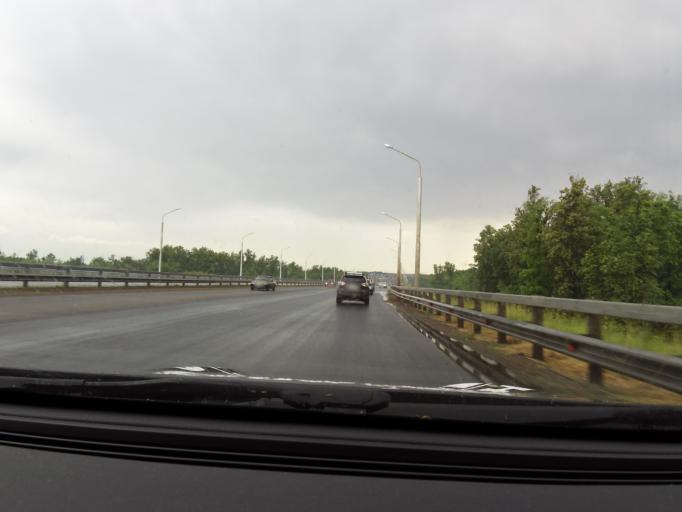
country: RU
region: Bashkortostan
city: Mikhaylovka
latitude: 54.7842
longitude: 55.9107
